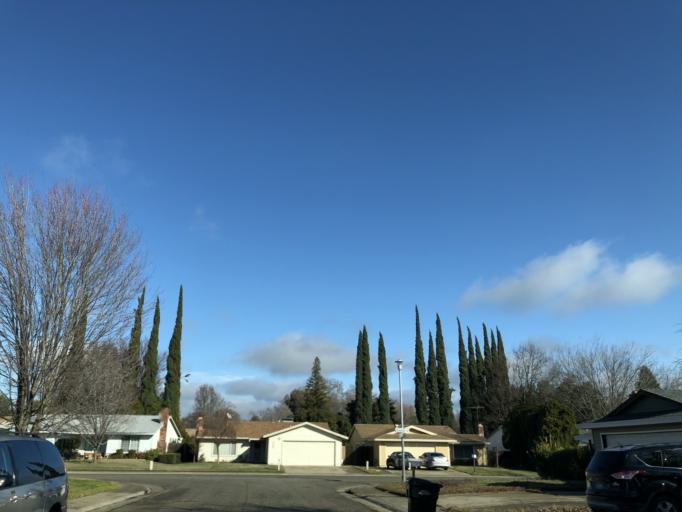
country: US
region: California
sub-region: Sacramento County
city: Rosemont
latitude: 38.5610
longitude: -121.3792
